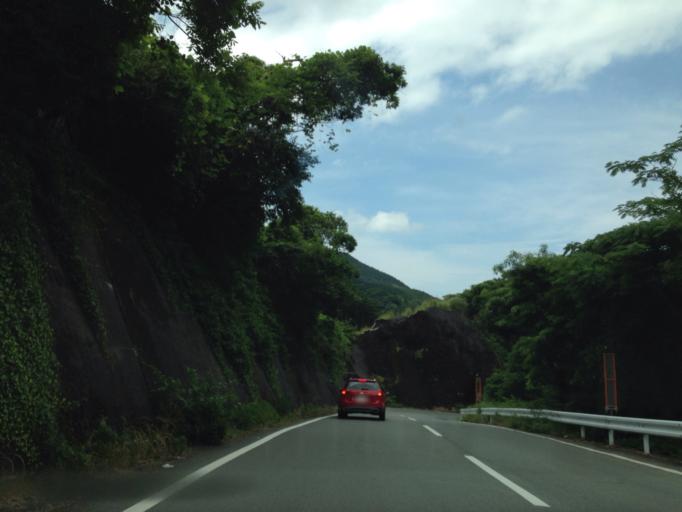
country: JP
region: Shizuoka
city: Heda
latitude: 34.9076
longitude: 138.8239
